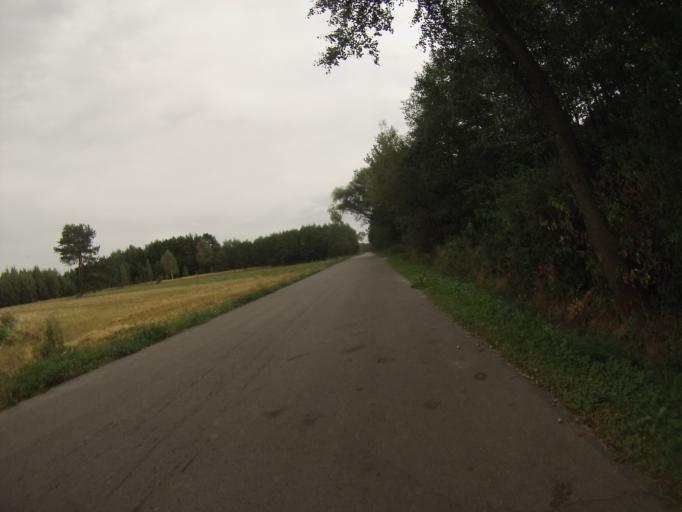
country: PL
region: Swietokrzyskie
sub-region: Powiat kielecki
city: Lagow
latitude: 50.7626
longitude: 21.0732
